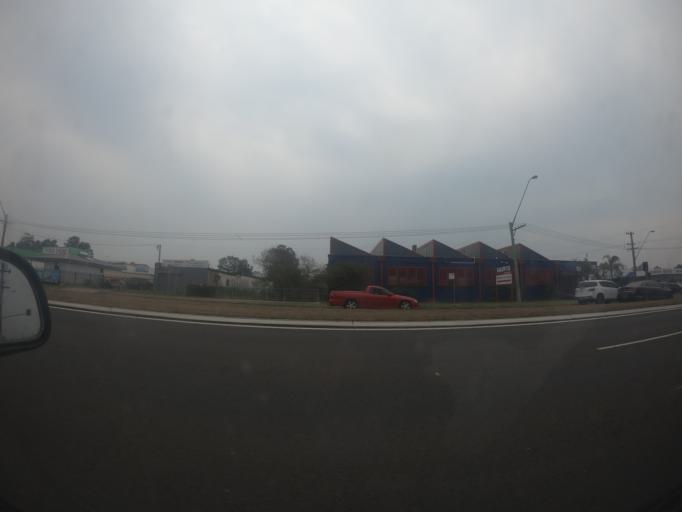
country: AU
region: New South Wales
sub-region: Shellharbour
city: Barrack Heights
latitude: -34.5582
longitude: 150.8597
